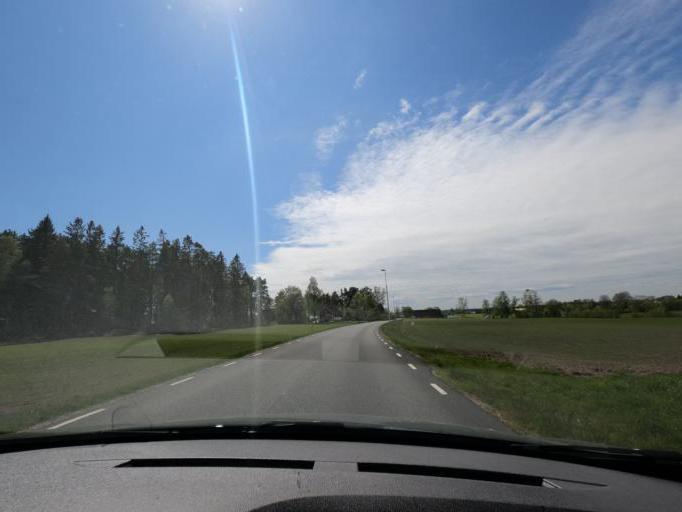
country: SE
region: Joenkoeping
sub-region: Varnamo Kommun
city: Bredaryd
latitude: 57.1377
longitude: 13.7118
